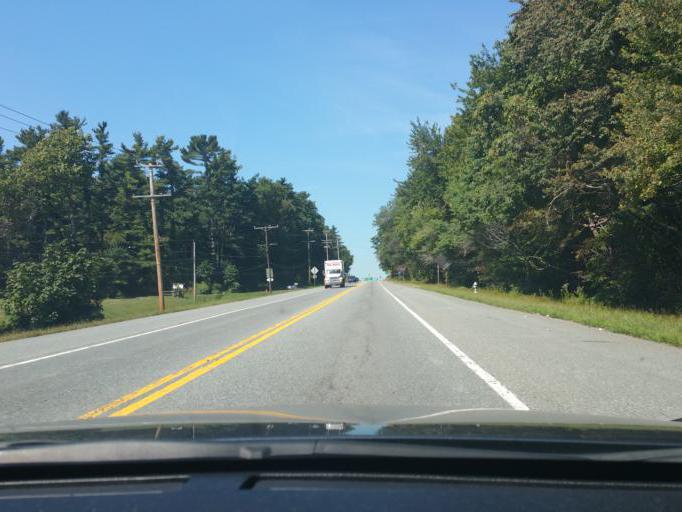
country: US
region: Maryland
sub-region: Harford County
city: Havre de Grace
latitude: 39.5651
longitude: -76.1255
